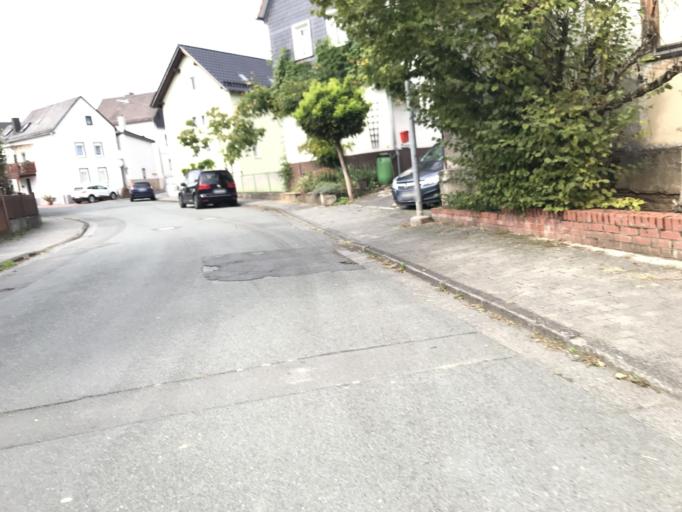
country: DE
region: Hesse
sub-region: Regierungsbezirk Giessen
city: Ehringshausen
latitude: 50.5999
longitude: 8.4168
